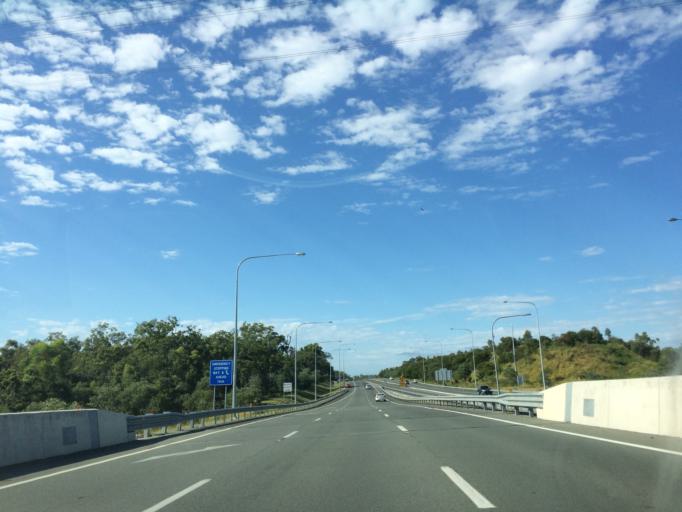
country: AU
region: Queensland
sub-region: Brisbane
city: Forest Lake
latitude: -27.6284
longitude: 152.9411
